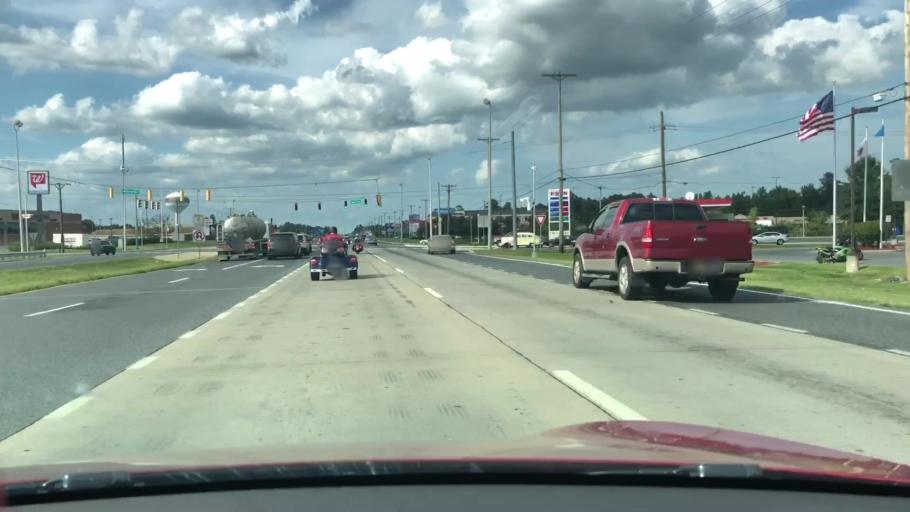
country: US
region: Delaware
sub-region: Sussex County
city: Seaford
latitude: 38.6598
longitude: -75.5939
